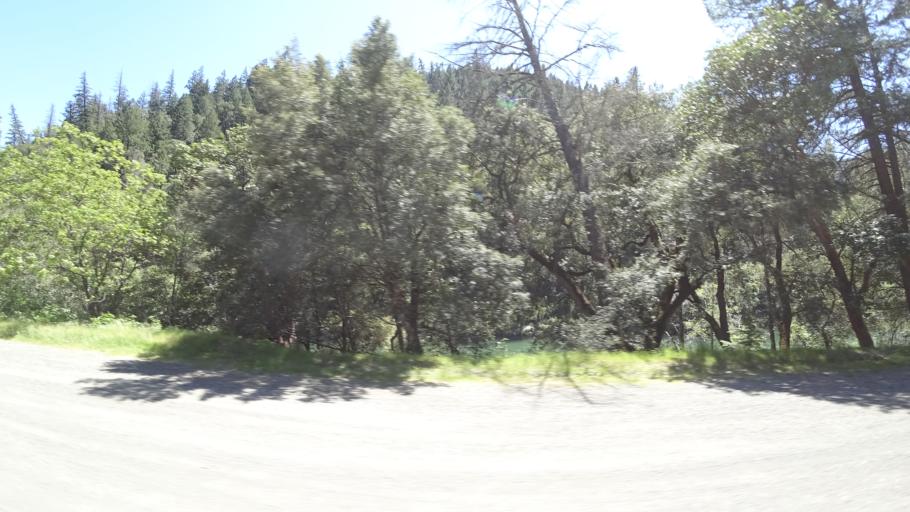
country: US
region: California
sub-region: Trinity County
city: Hayfork
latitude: 40.7774
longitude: -123.3201
